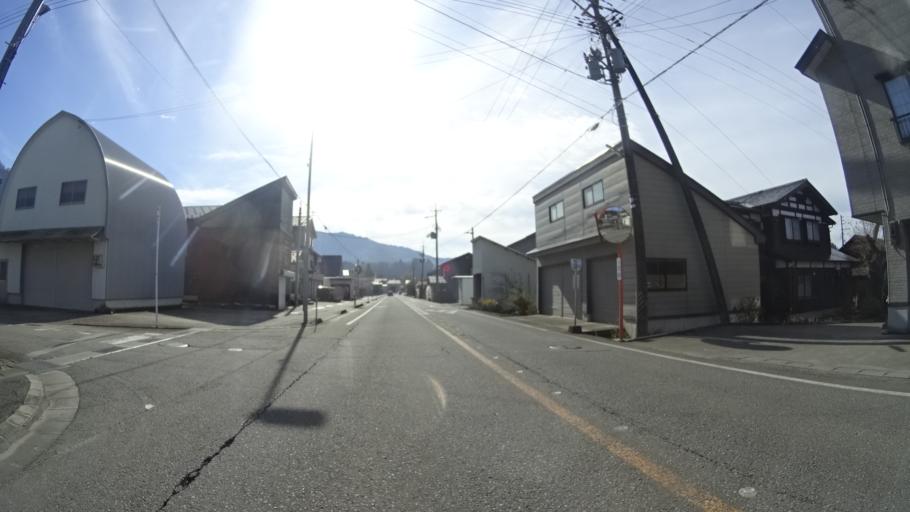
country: JP
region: Niigata
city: Muikamachi
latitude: 37.1432
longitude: 138.9584
